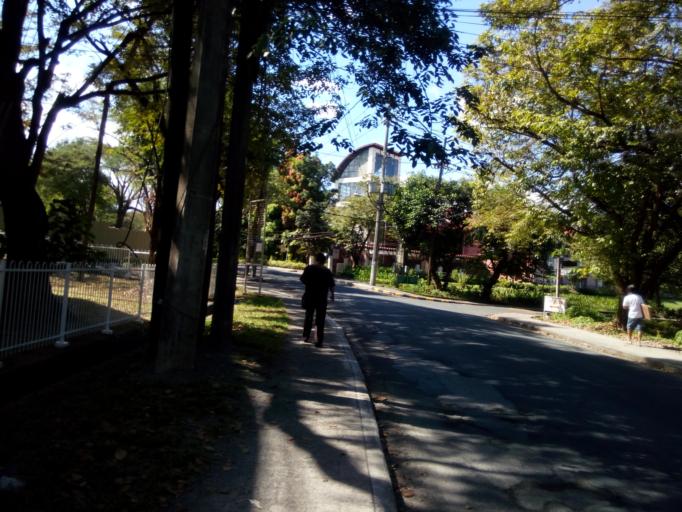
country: PH
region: Metro Manila
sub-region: Quezon City
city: Quezon City
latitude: 14.6520
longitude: 121.0672
